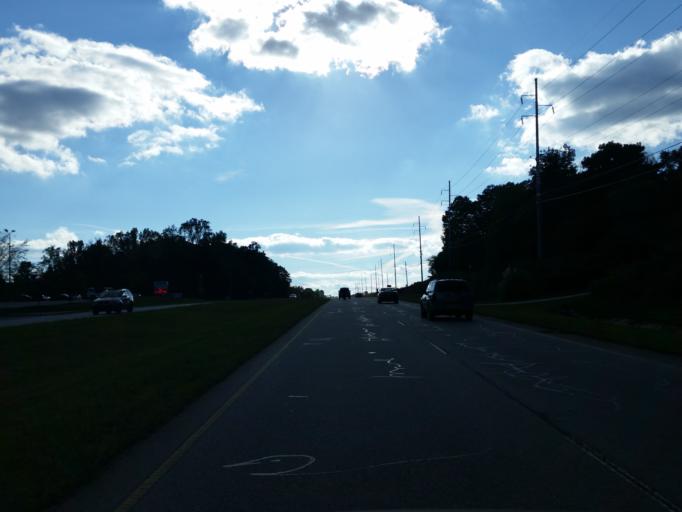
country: US
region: Georgia
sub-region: Paulding County
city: Hiram
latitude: 33.9224
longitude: -84.7573
